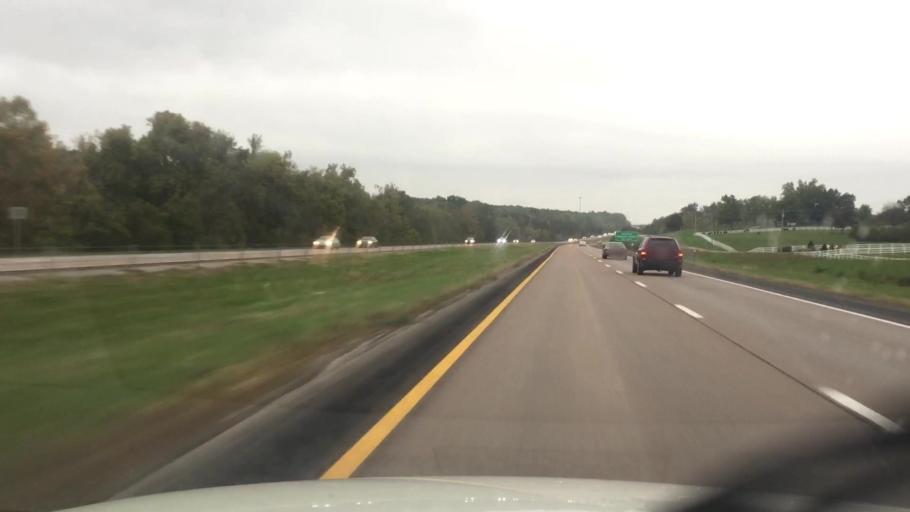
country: US
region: Missouri
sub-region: Boone County
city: Ashland
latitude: 38.8171
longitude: -92.2513
